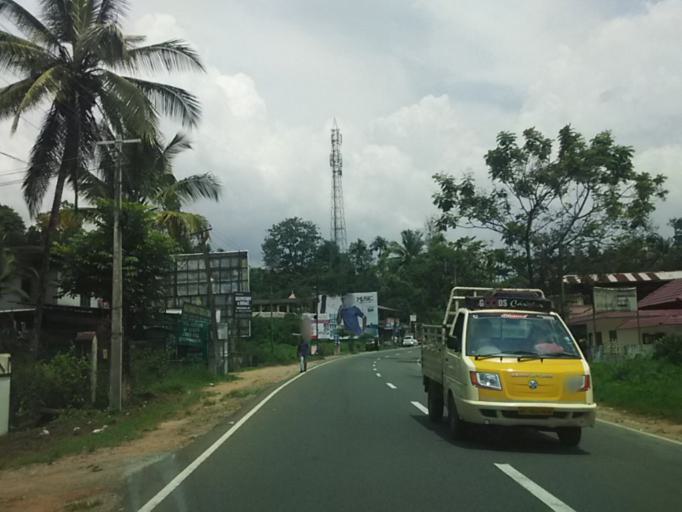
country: IN
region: Kerala
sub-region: Wayanad
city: Kalpetta
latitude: 11.5733
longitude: 76.0541
